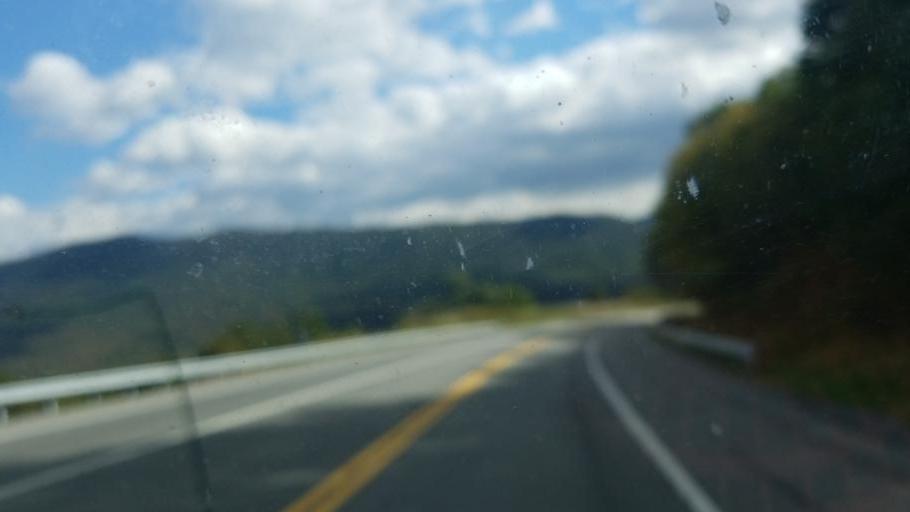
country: US
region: Pennsylvania
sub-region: Fulton County
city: McConnellsburg
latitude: 39.9368
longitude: -77.9239
